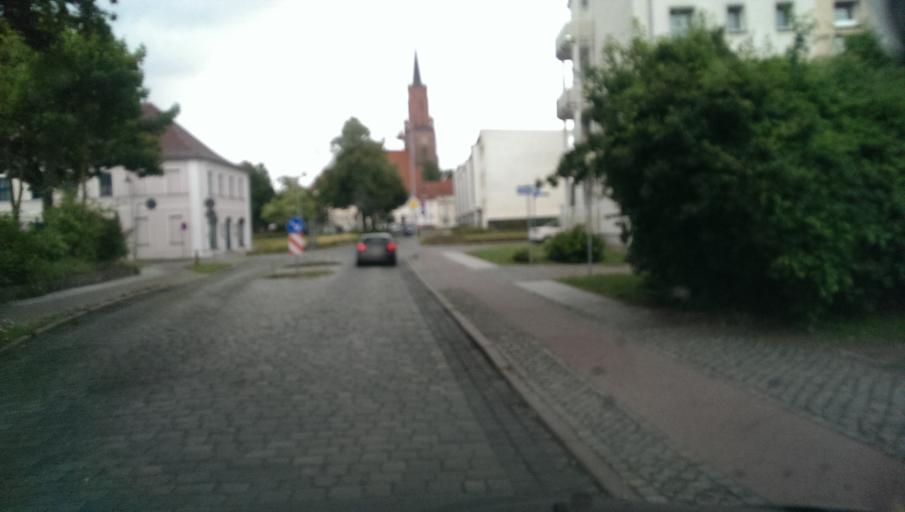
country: DE
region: Brandenburg
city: Rathenow
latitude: 52.6091
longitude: 12.3331
